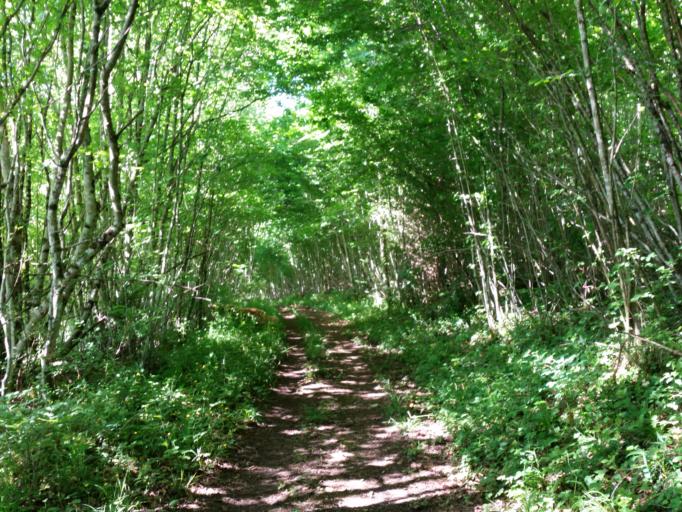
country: FR
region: Franche-Comte
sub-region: Departement du Doubs
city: Quingey
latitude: 47.0350
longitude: 5.9681
